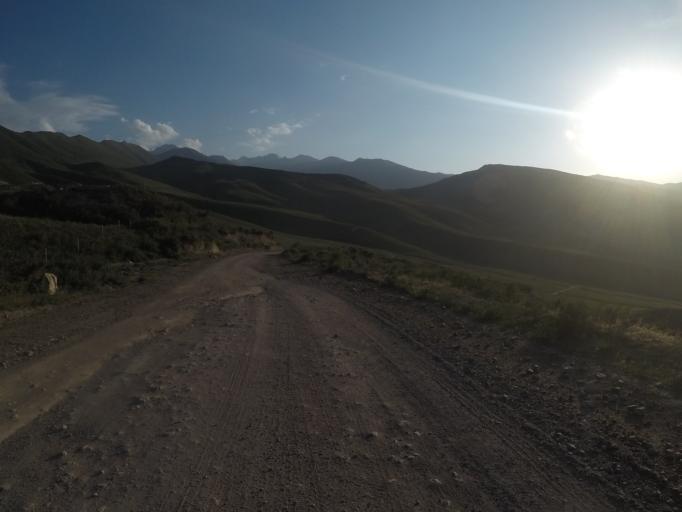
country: KG
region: Chuy
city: Bishkek
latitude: 42.6567
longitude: 74.6617
